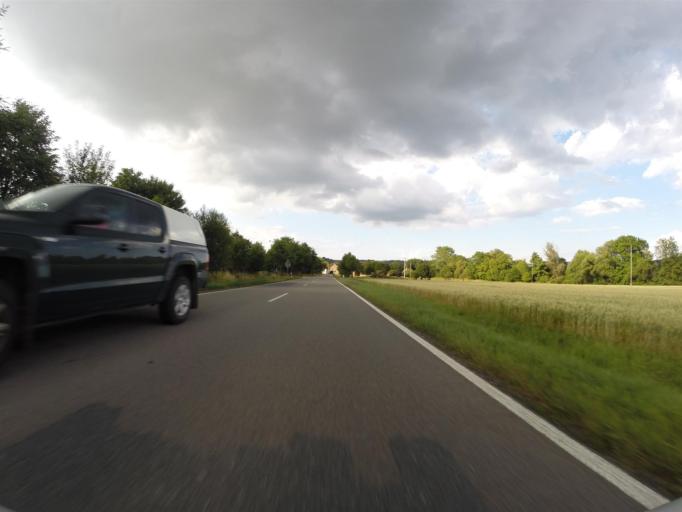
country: DE
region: Thuringia
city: Barchfeld
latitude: 50.8009
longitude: 11.1626
